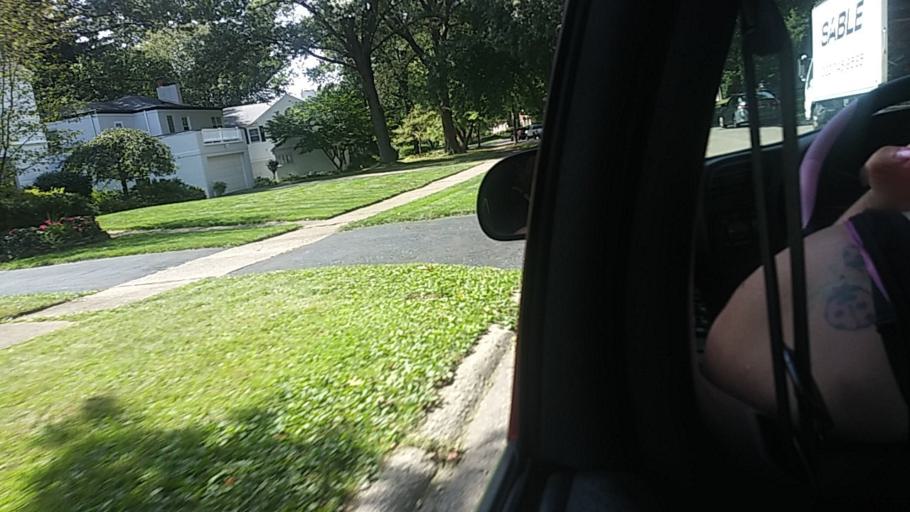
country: US
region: Ohio
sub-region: Summit County
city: Akron
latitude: 41.1008
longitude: -81.5600
